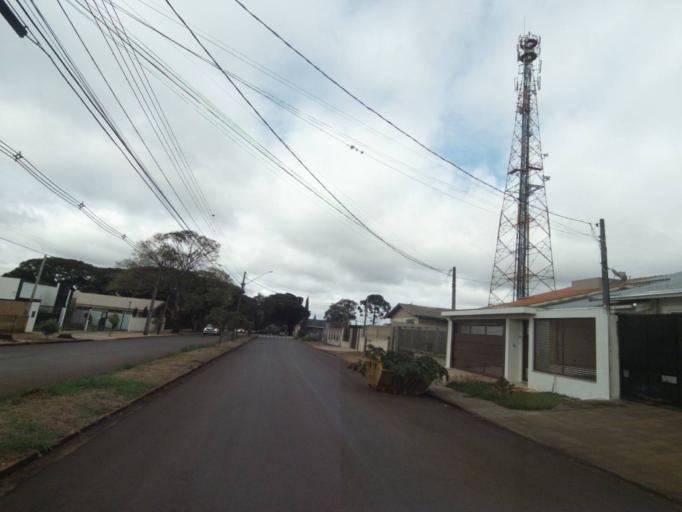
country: BR
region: Parana
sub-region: Campo Mourao
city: Campo Mourao
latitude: -24.0475
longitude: -52.3748
